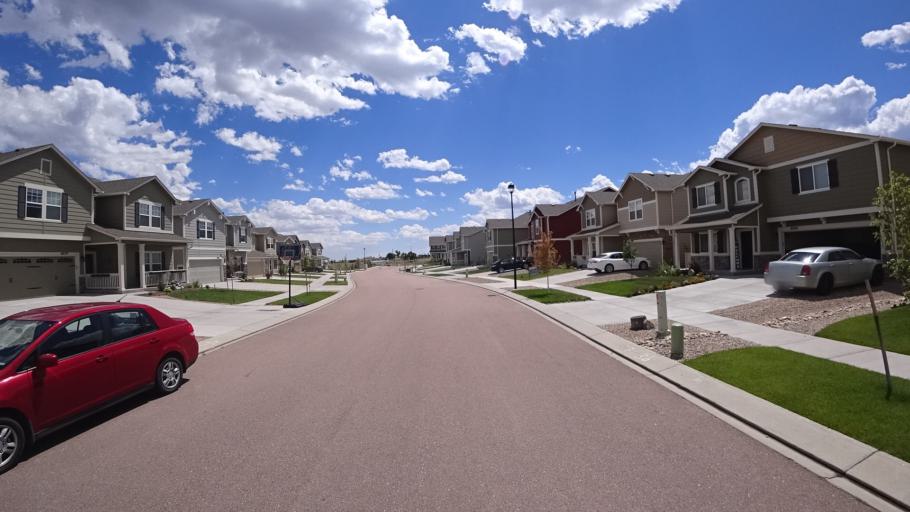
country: US
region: Colorado
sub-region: El Paso County
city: Black Forest
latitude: 38.9501
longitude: -104.7038
